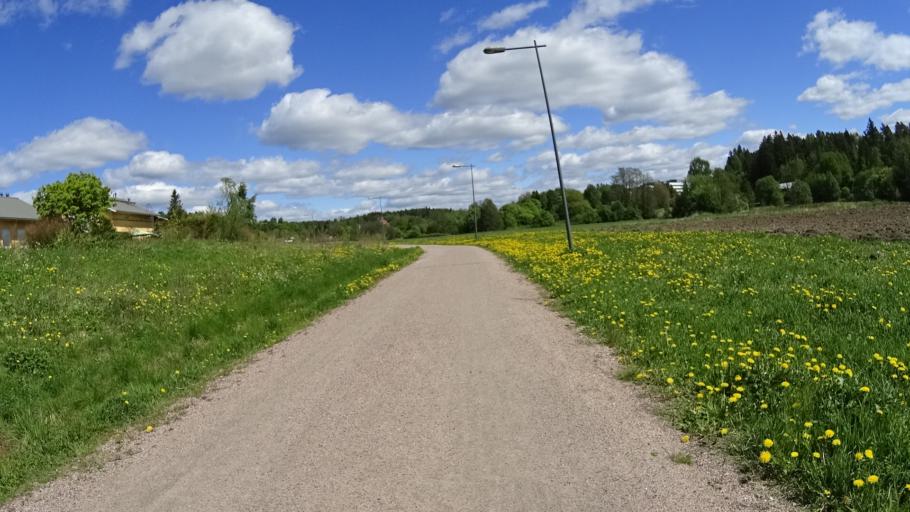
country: FI
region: Uusimaa
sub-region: Helsinki
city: Espoo
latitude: 60.2187
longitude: 24.6722
